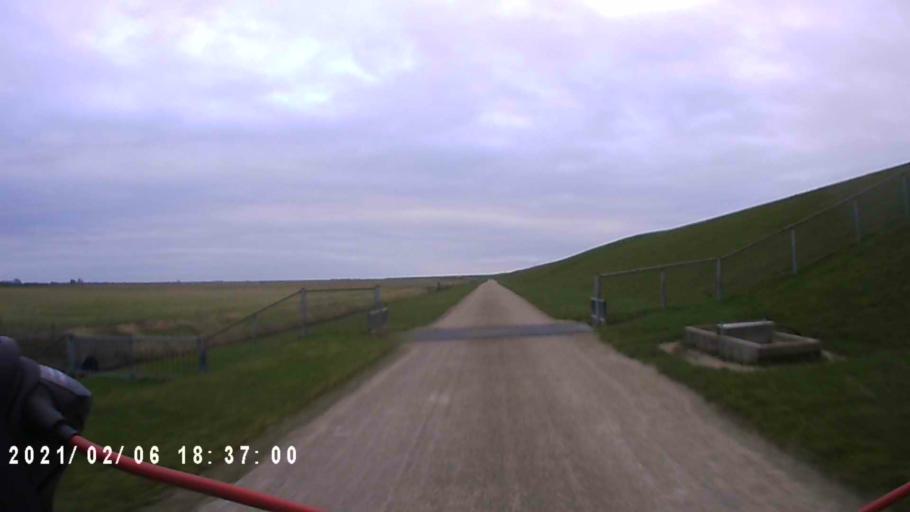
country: NL
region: Groningen
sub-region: Gemeente Bedum
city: Bedum
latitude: 53.4457
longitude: 6.6264
